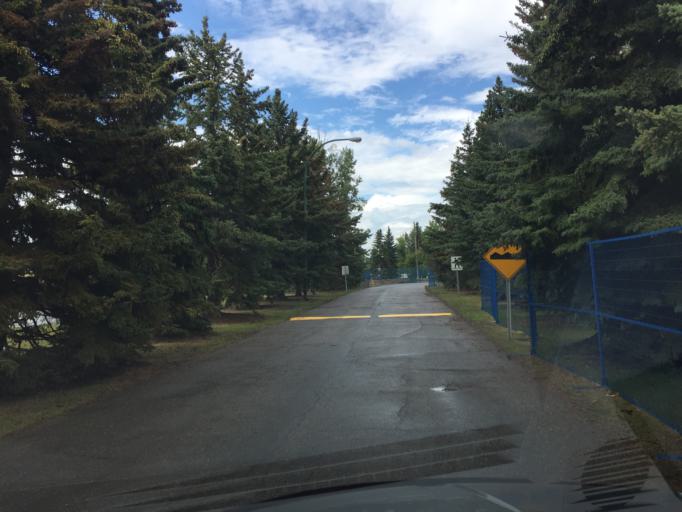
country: CA
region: Alberta
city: Calgary
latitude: 51.0180
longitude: -114.1279
